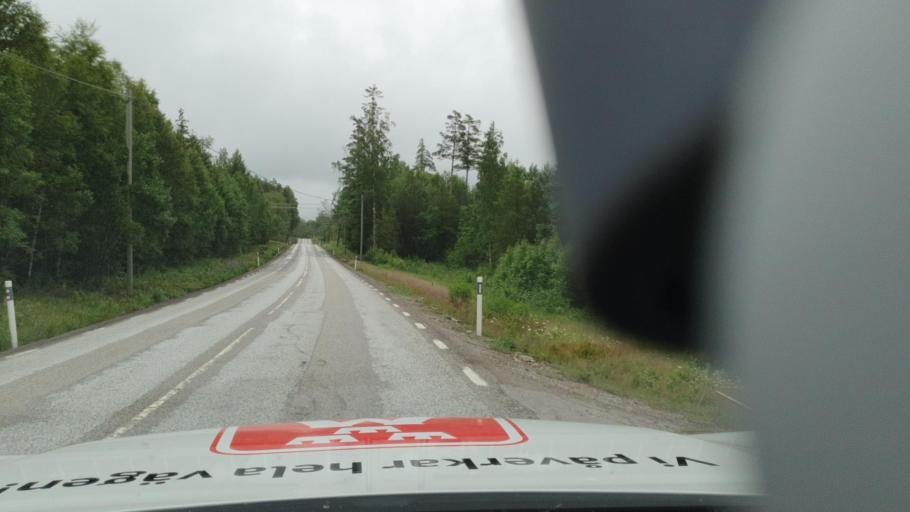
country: SE
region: Vaermland
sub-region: Kristinehamns Kommun
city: Bjorneborg
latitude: 59.2414
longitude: 14.2229
